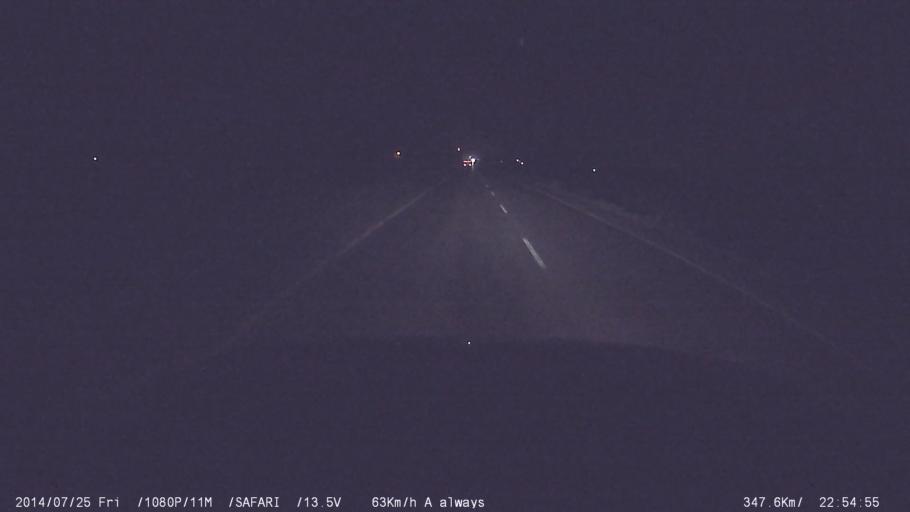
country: IN
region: Tamil Nadu
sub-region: Coimbatore
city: Singanallur
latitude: 10.9919
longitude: 77.0575
